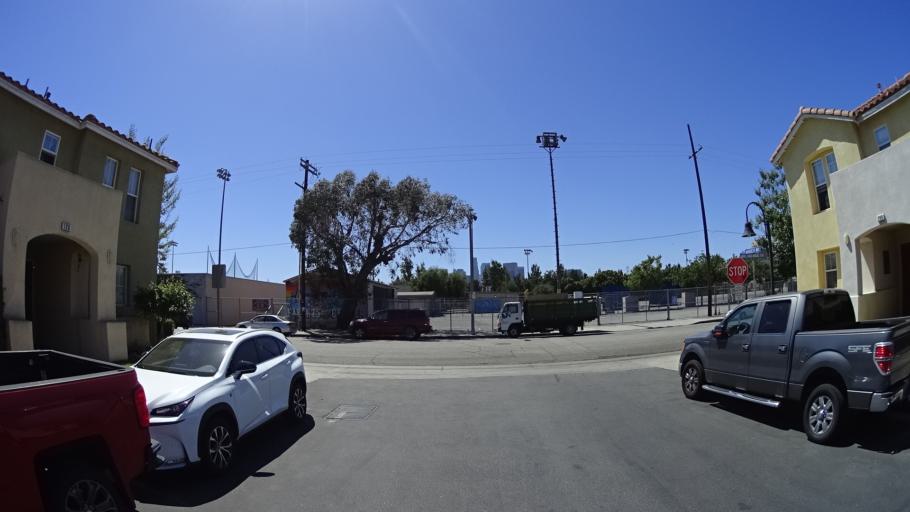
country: US
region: California
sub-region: Los Angeles County
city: Los Angeles
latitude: 34.0486
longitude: -118.2237
